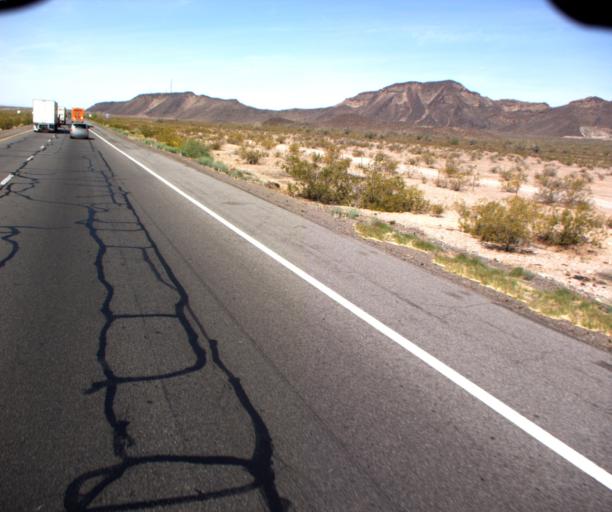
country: US
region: Arizona
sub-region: Maricopa County
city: Buckeye
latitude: 33.5218
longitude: -113.0750
